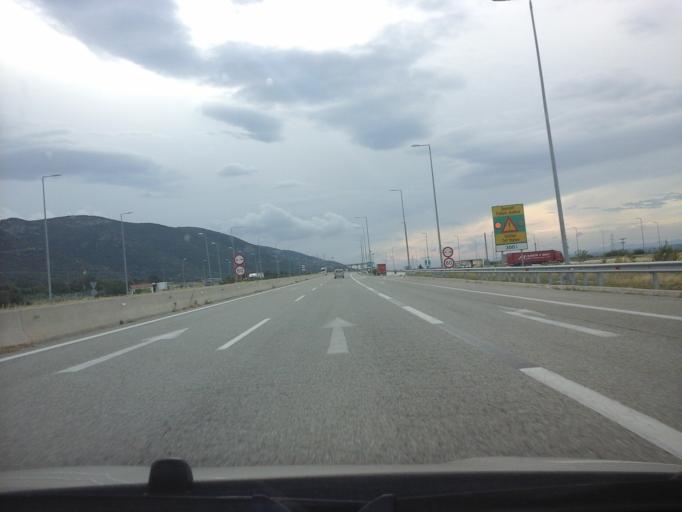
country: GR
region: East Macedonia and Thrace
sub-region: Nomos Xanthis
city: Selero
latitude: 41.1204
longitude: 25.0736
